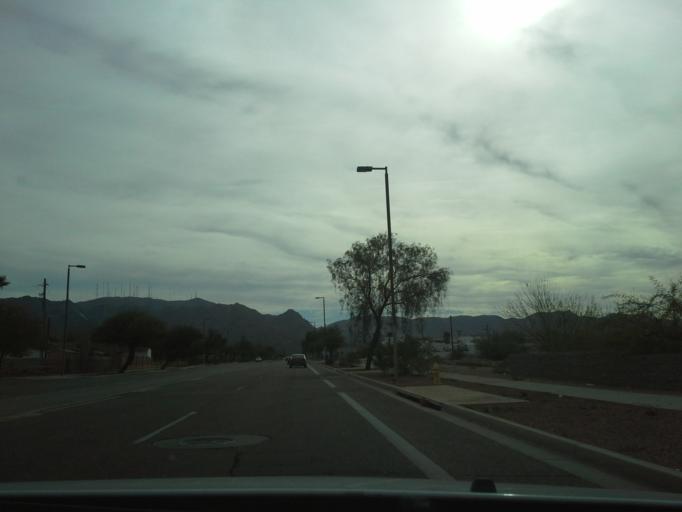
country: US
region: Arizona
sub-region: Maricopa County
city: Phoenix
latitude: 33.3688
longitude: -112.0733
